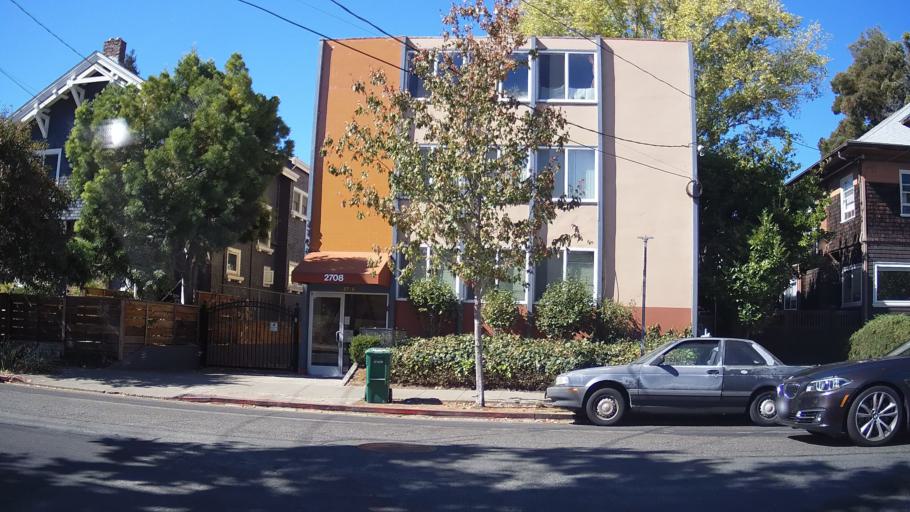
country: US
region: California
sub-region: Alameda County
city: Berkeley
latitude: 37.8615
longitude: -122.2533
